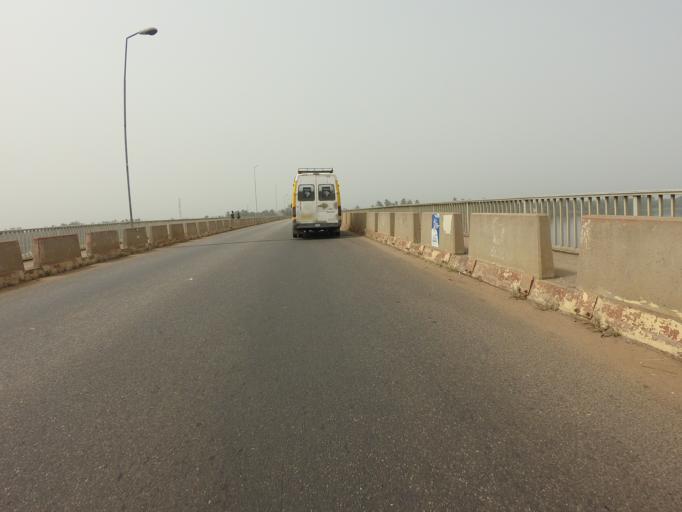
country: GH
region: Volta
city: Anloga
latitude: 5.9953
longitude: 0.5855
